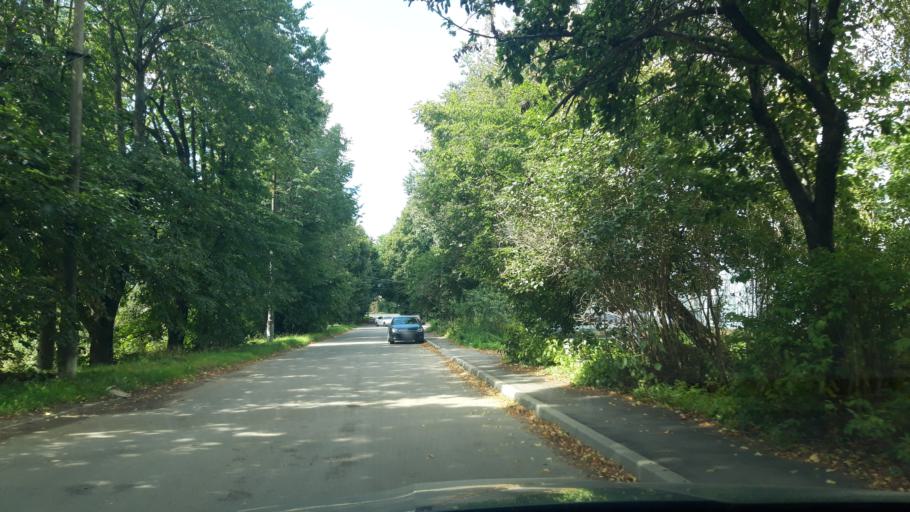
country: RU
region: Moskovskaya
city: Chashnikovo
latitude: 56.0343
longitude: 37.1676
